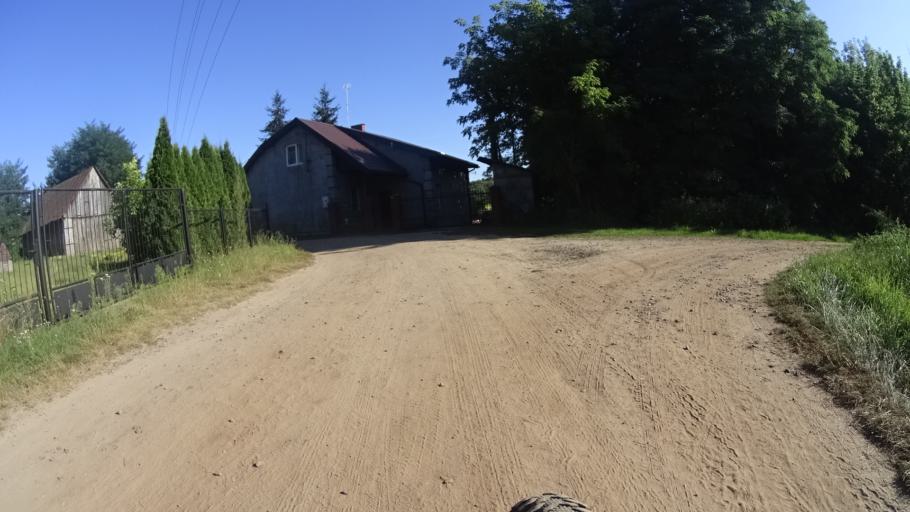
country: PL
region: Masovian Voivodeship
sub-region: Powiat bialobrzeski
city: Wysmierzyce
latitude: 51.6617
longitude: 20.8469
